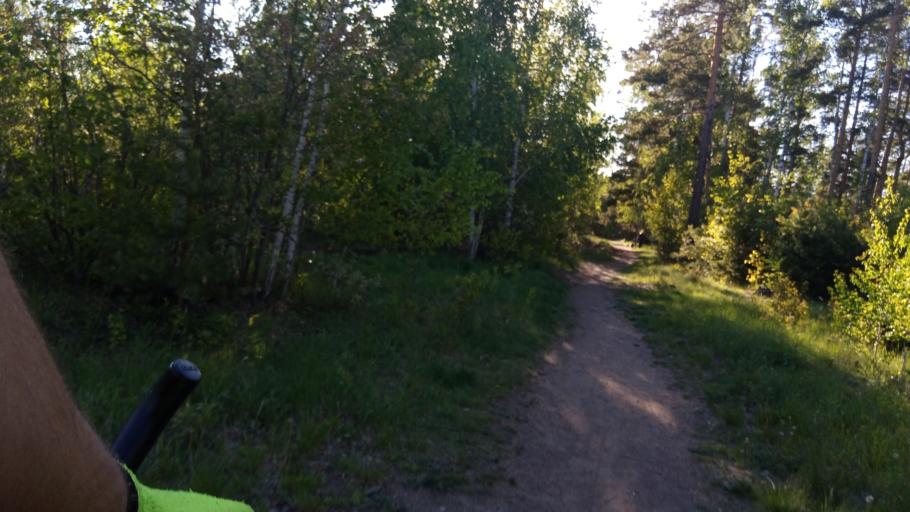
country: RU
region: Chelyabinsk
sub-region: Gorod Chelyabinsk
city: Chelyabinsk
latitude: 55.1262
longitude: 61.3438
